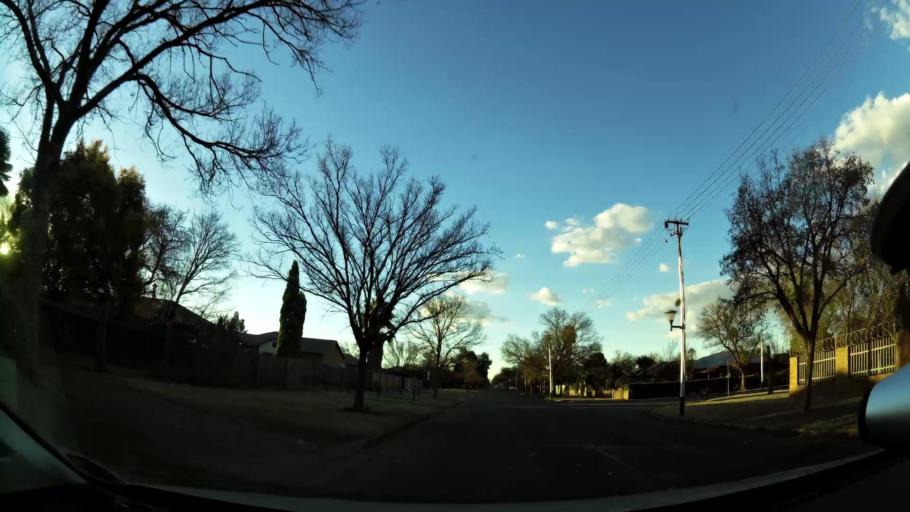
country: ZA
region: North-West
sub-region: Dr Kenneth Kaunda District Municipality
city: Potchefstroom
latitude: -26.7329
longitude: 27.0893
